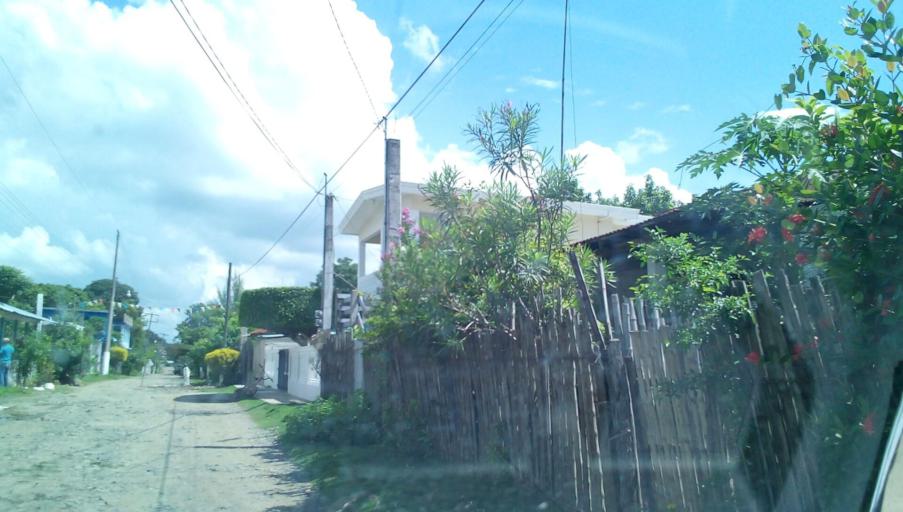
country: MX
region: Veracruz
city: Tamalin
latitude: 21.3658
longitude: -97.8012
